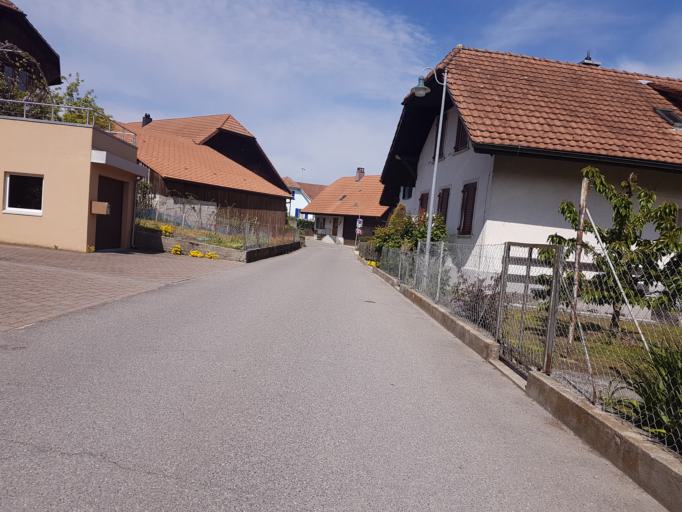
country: CH
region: Bern
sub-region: Seeland District
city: Tauffelen
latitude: 47.0467
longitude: 7.1528
